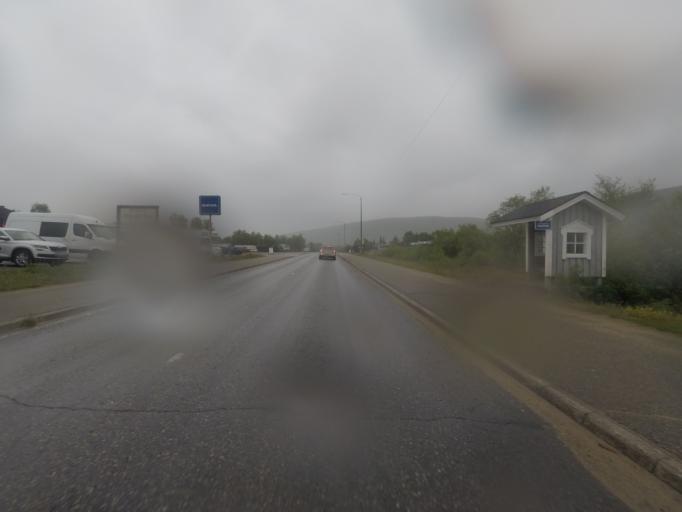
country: FI
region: Lapland
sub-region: Pohjois-Lappi
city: Utsjoki
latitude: 69.9077
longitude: 27.0263
